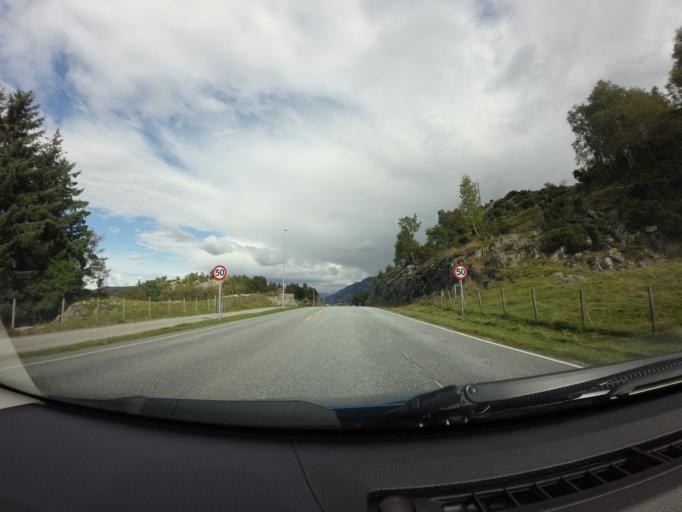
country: NO
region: Rogaland
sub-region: Forsand
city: Forsand
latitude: 58.8911
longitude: 6.0483
